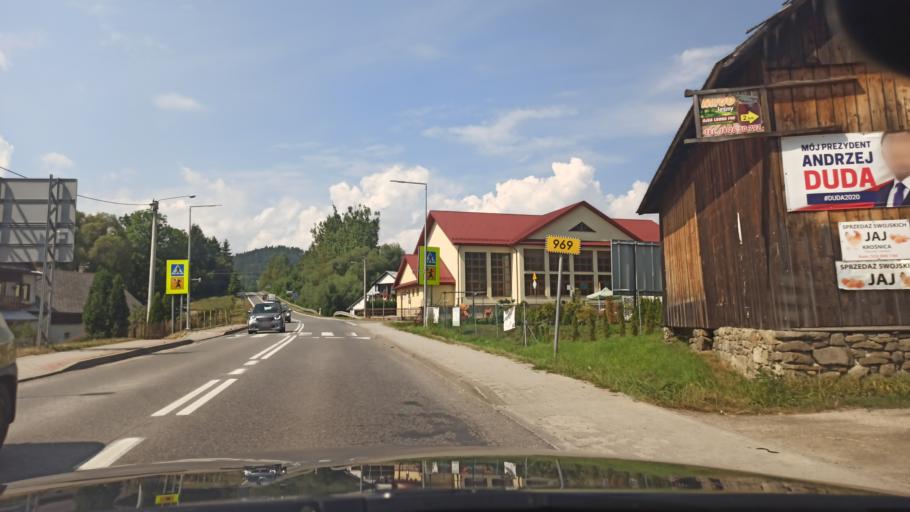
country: PL
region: Lesser Poland Voivodeship
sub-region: Powiat nowotarski
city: Krosnica
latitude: 49.4473
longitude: 20.3395
